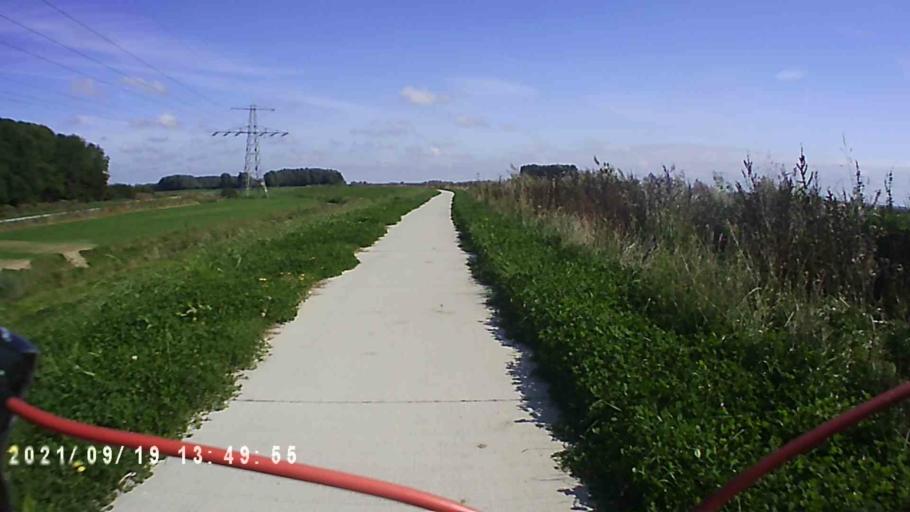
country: NL
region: Groningen
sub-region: Gemeente  Oldambt
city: Winschoten
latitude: 53.1335
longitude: 7.0589
